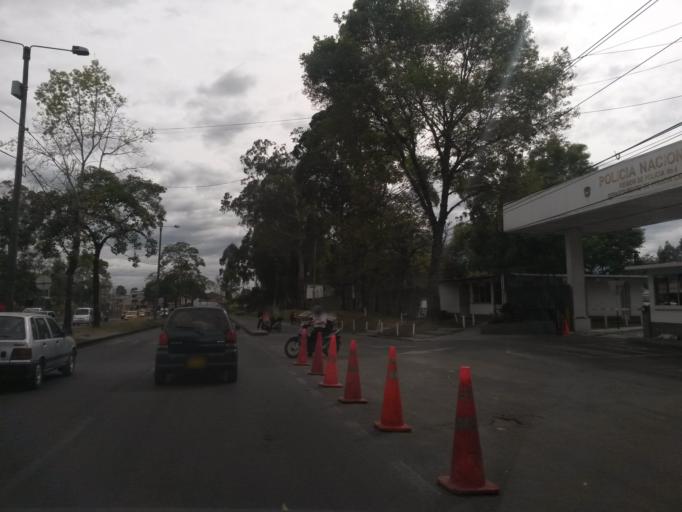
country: CO
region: Cauca
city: Popayan
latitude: 2.4488
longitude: -76.6117
